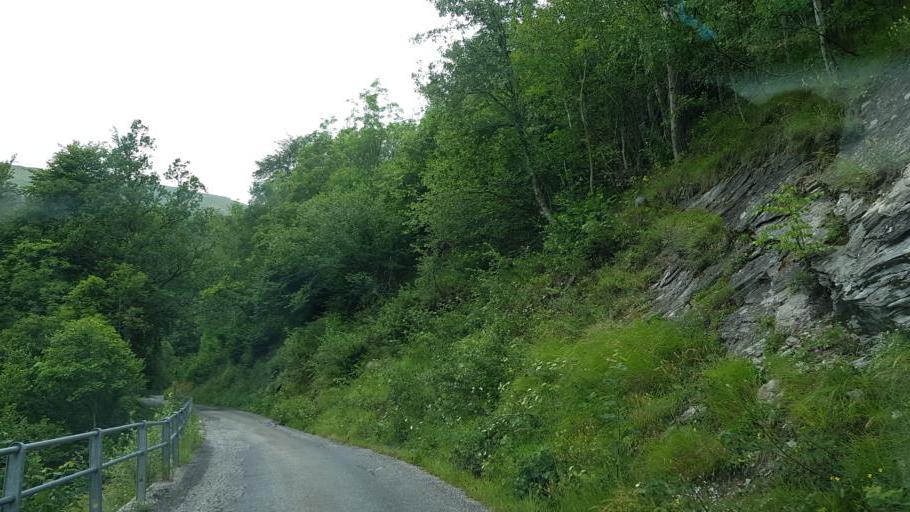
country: IT
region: Piedmont
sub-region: Provincia di Cuneo
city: Stroppo
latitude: 44.5189
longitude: 7.1288
